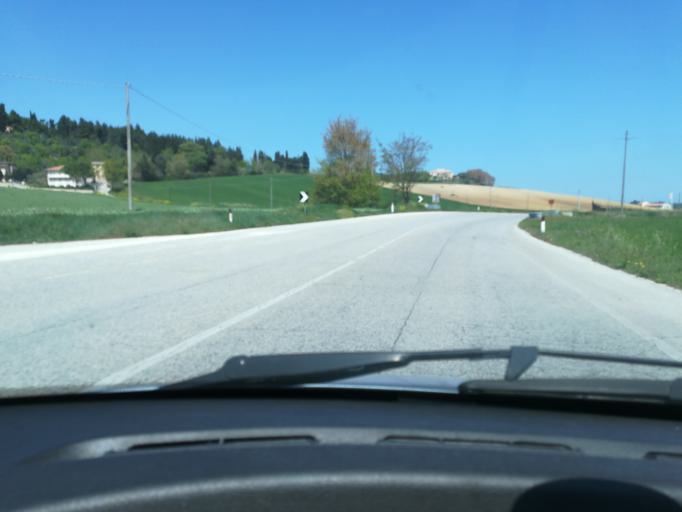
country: IT
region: The Marches
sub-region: Provincia di Ancona
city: Villa Musone
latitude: 43.4614
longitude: 13.5982
